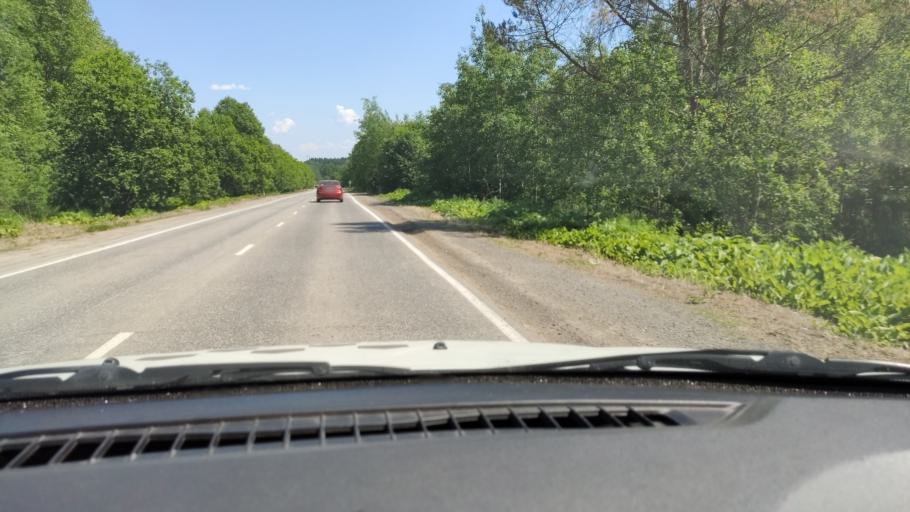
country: RU
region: Perm
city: Novyye Lyady
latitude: 58.0239
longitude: 56.6668
